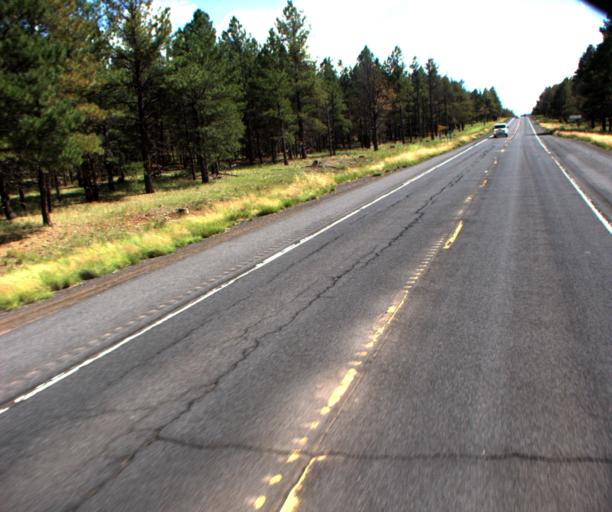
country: US
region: Arizona
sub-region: Coconino County
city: Williams
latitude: 35.2824
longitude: -112.1460
